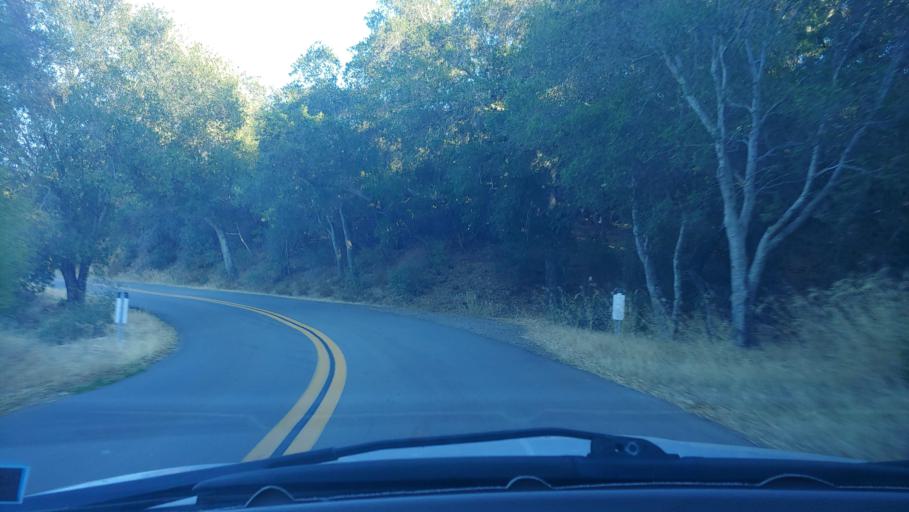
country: US
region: California
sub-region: Santa Barbara County
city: Goleta
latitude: 34.5349
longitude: -119.8458
